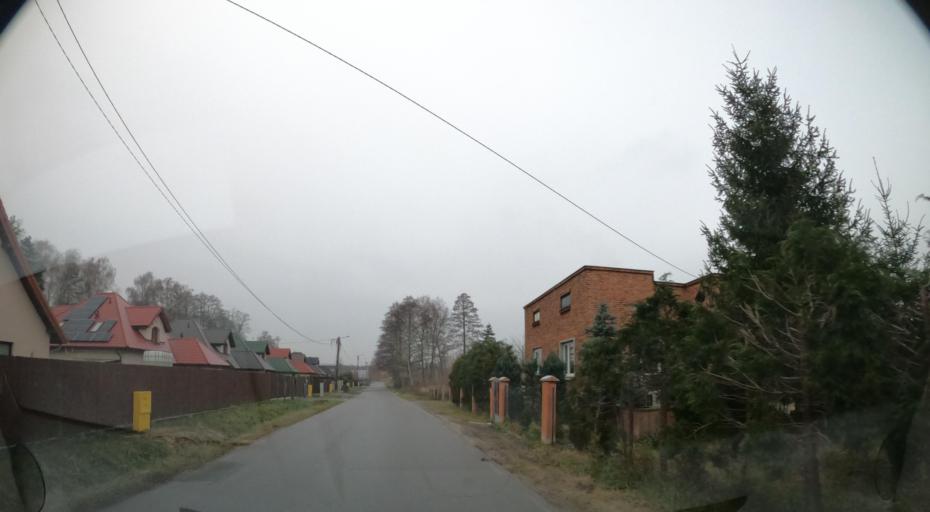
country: PL
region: Masovian Voivodeship
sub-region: Powiat radomski
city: Jastrzebia
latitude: 51.4251
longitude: 21.2285
